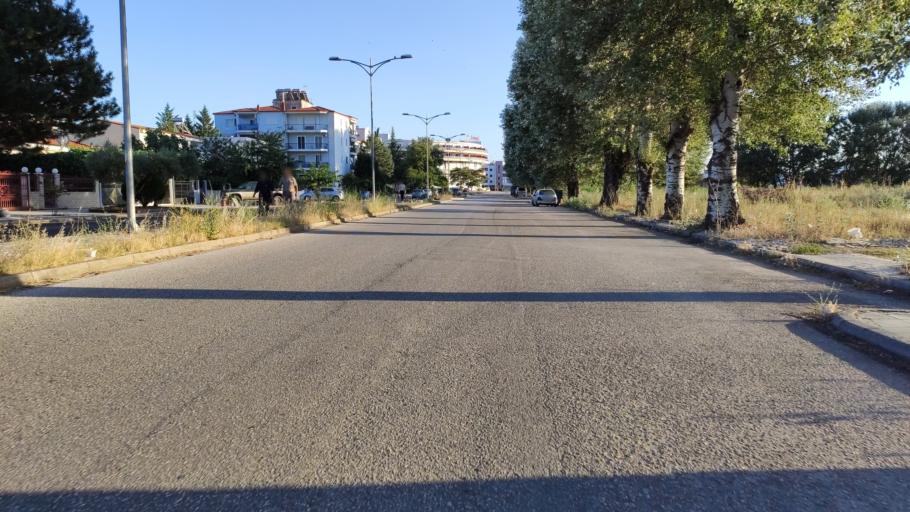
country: GR
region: East Macedonia and Thrace
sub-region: Nomos Rodopis
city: Komotini
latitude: 41.1279
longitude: 25.3948
